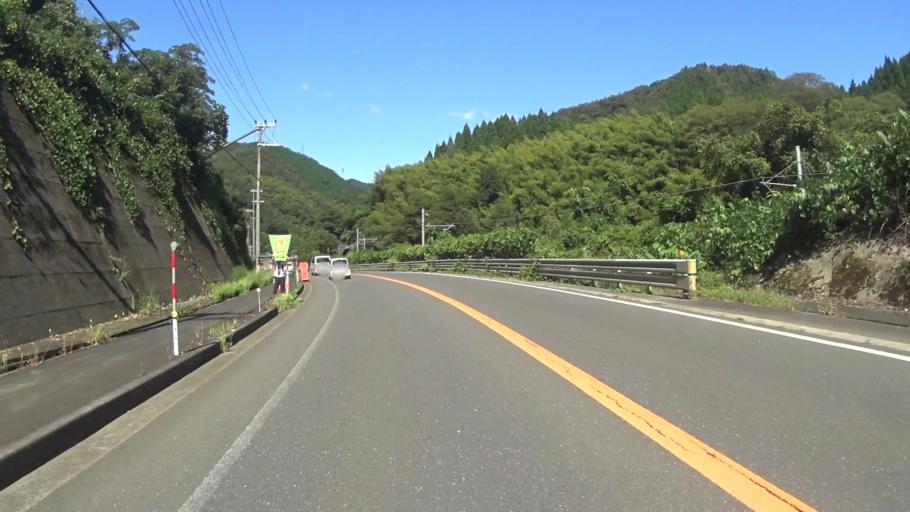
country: JP
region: Kyoto
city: Maizuru
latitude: 35.3778
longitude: 135.3186
